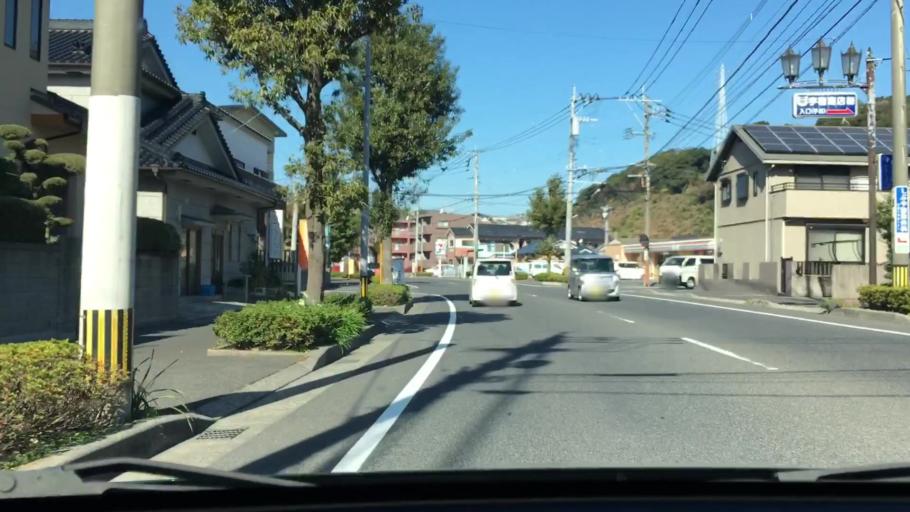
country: JP
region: Kagoshima
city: Kagoshima-shi
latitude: 31.5479
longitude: 130.5331
